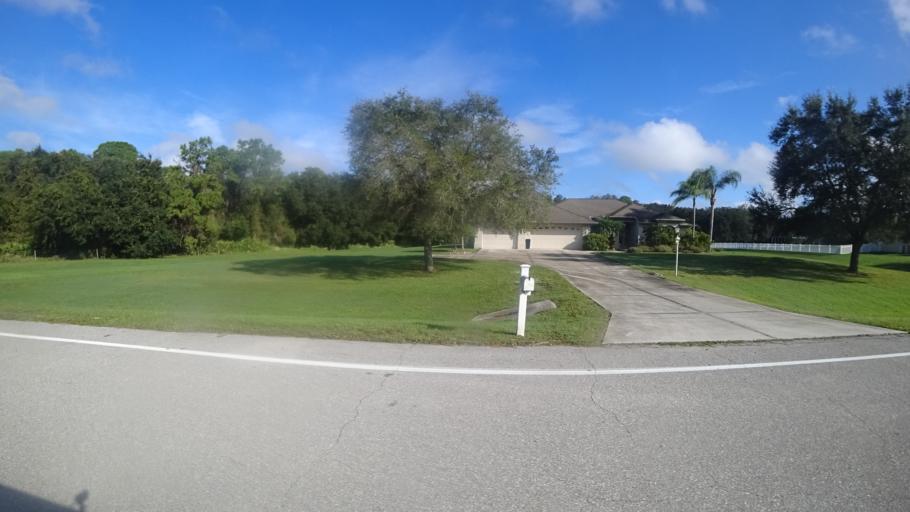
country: US
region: Florida
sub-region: Hillsborough County
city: Sun City Center
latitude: 27.5598
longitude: -82.3672
